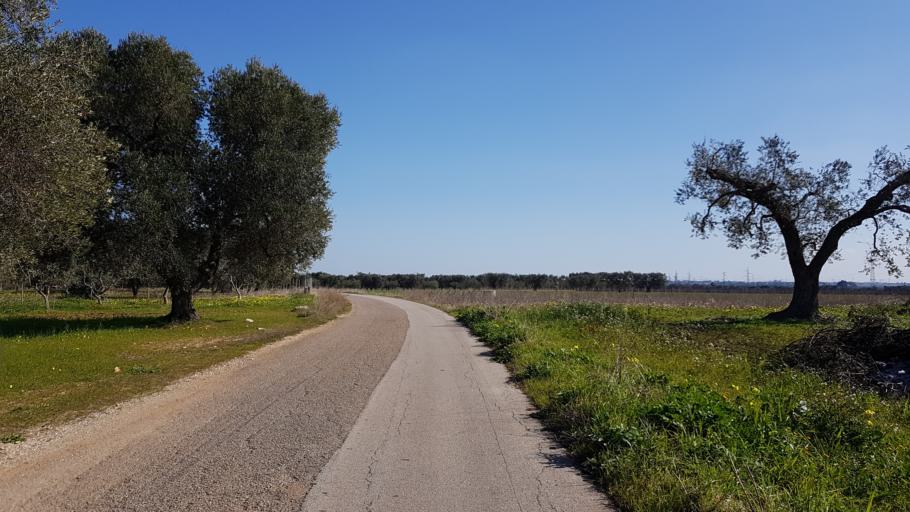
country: IT
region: Apulia
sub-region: Provincia di Brindisi
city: Mesagne
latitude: 40.6191
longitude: 17.8409
